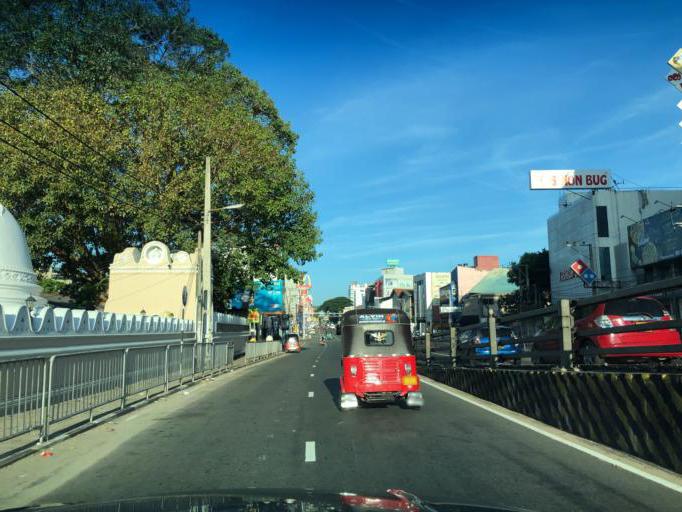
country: LK
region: Western
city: Sri Jayewardenepura Kotte
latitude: 6.8701
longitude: 79.8875
